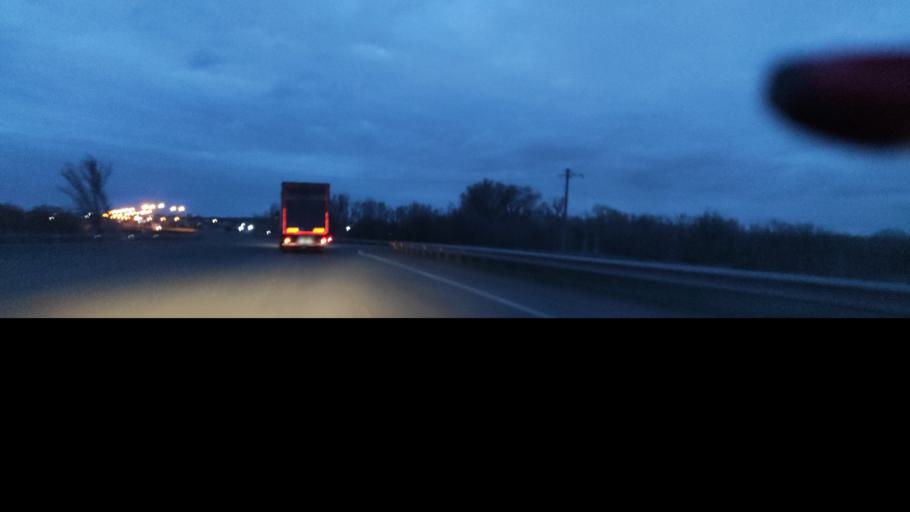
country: RU
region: Orenburg
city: Tatarskaya Kargala
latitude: 51.9397
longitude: 55.1766
